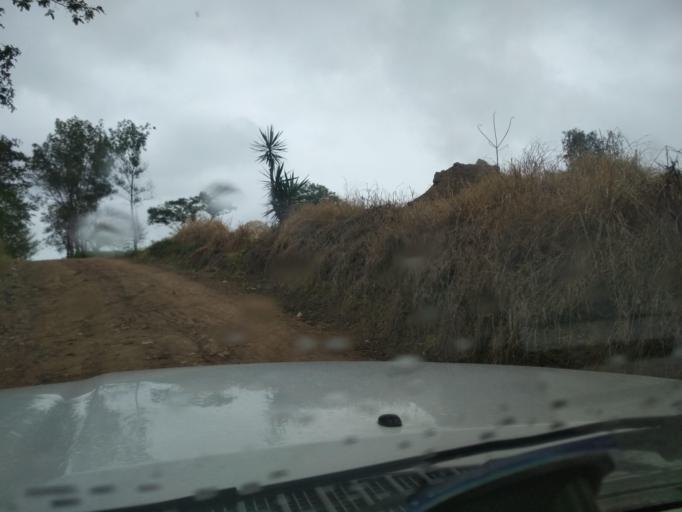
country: MX
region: Veracruz
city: El Castillo
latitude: 19.5378
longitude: -96.8287
